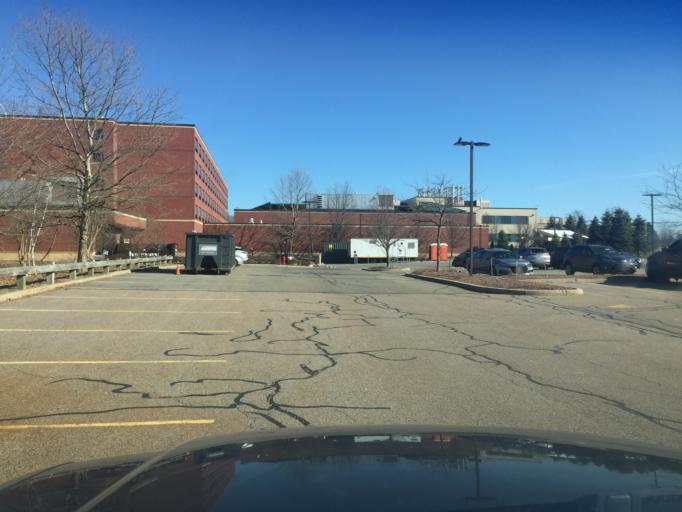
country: US
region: Massachusetts
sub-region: Norfolk County
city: Norwood
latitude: 42.1759
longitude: -71.1965
